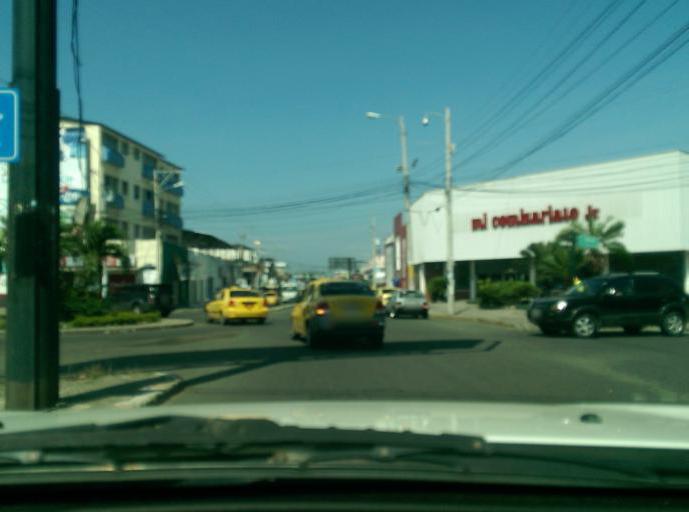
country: EC
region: Manabi
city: Manta
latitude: -0.9448
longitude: -80.7341
